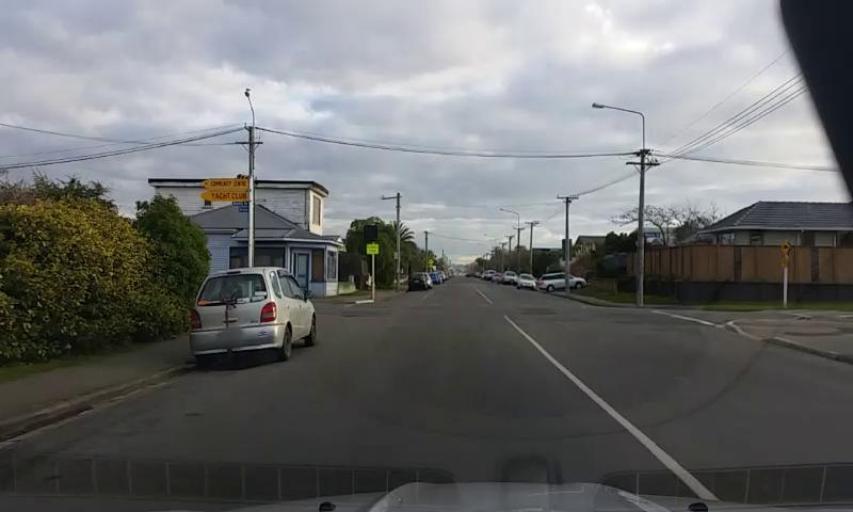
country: NZ
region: Canterbury
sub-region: Christchurch City
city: Christchurch
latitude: -43.5280
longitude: 172.7347
